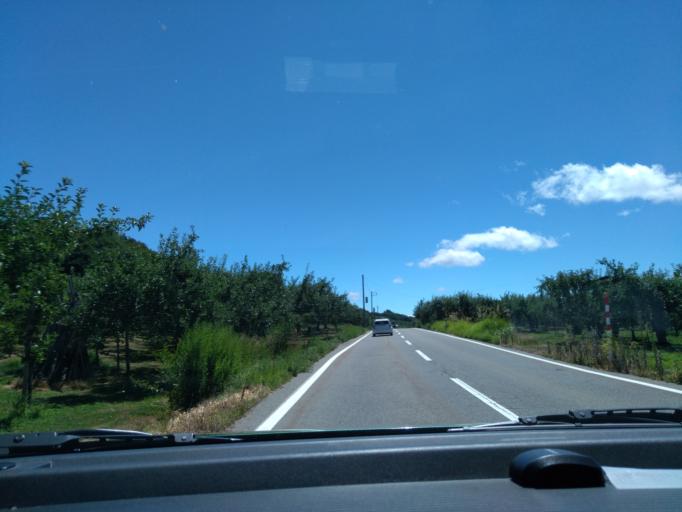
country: JP
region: Akita
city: Yokotemachi
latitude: 39.2392
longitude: 140.5628
